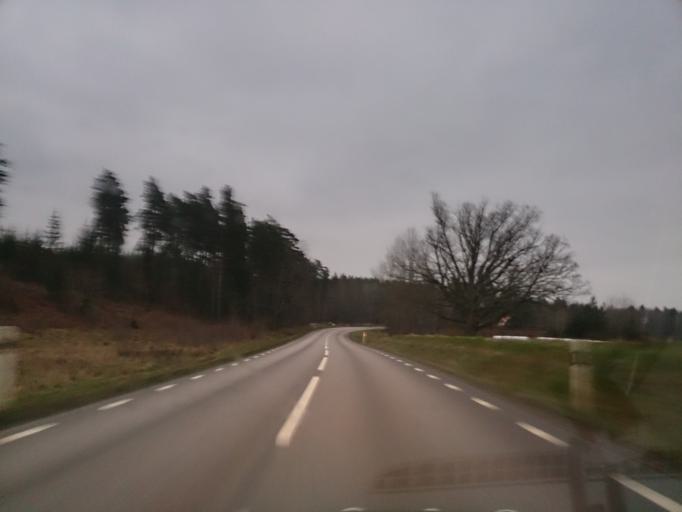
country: SE
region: OEstergoetland
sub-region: Linkopings Kommun
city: Sturefors
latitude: 58.3086
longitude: 15.8808
